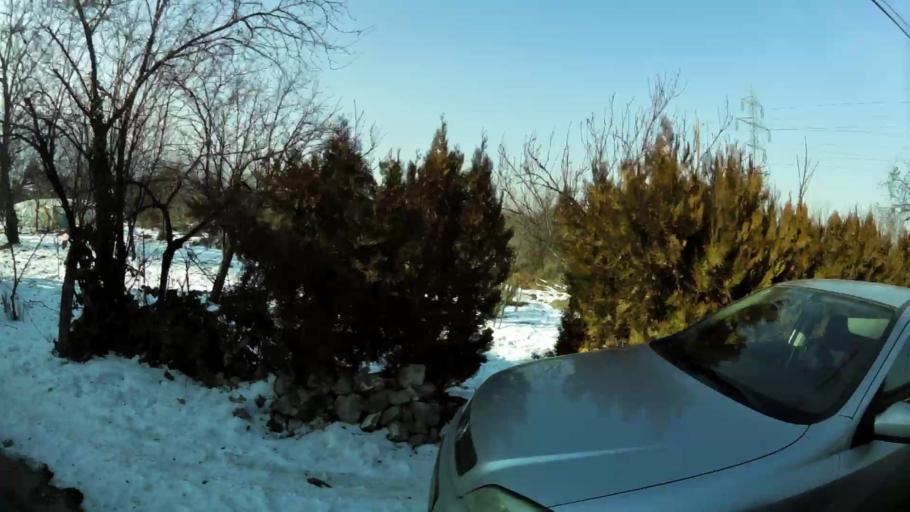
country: MK
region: Kisela Voda
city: Usje
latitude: 41.9719
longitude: 21.4526
